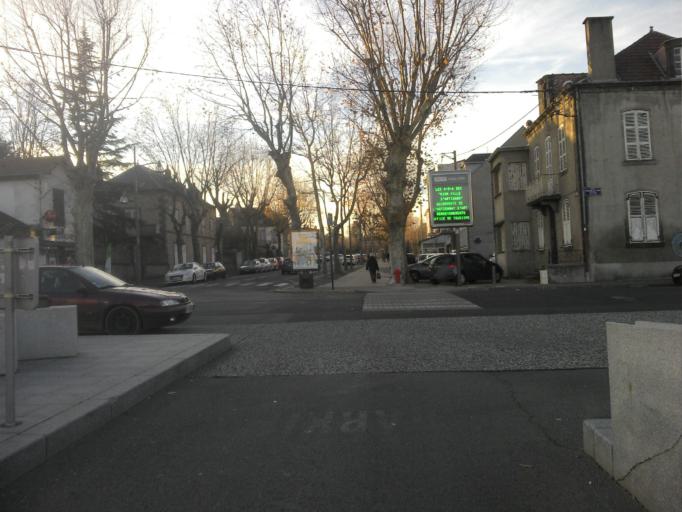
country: FR
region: Auvergne
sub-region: Departement du Puy-de-Dome
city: Riom
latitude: 45.8901
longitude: 3.1201
